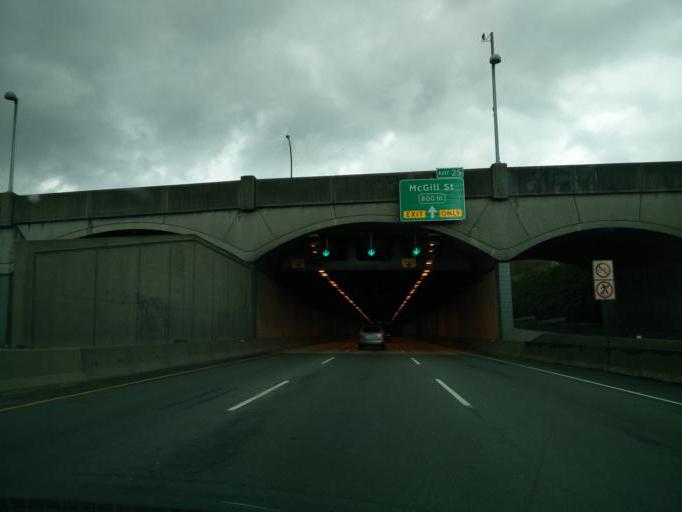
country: CA
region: British Columbia
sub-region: Fraser Valley Regional District
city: North Vancouver
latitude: 49.2771
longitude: -123.0315
